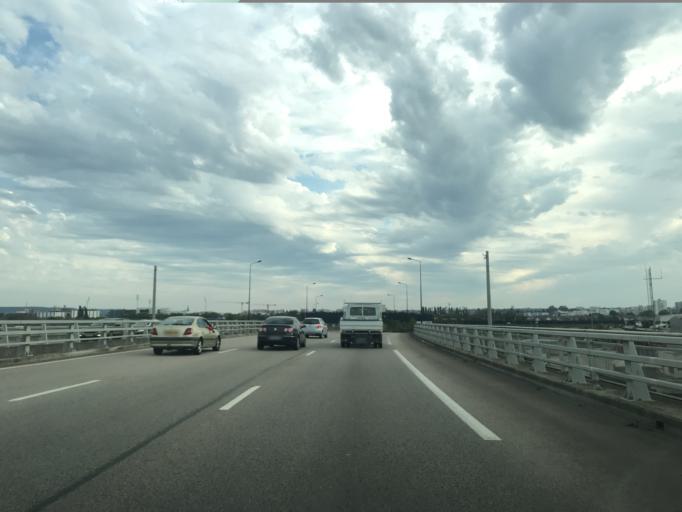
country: FR
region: Haute-Normandie
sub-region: Departement de la Seine-Maritime
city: Le Petit-Quevilly
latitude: 49.4404
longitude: 1.0658
